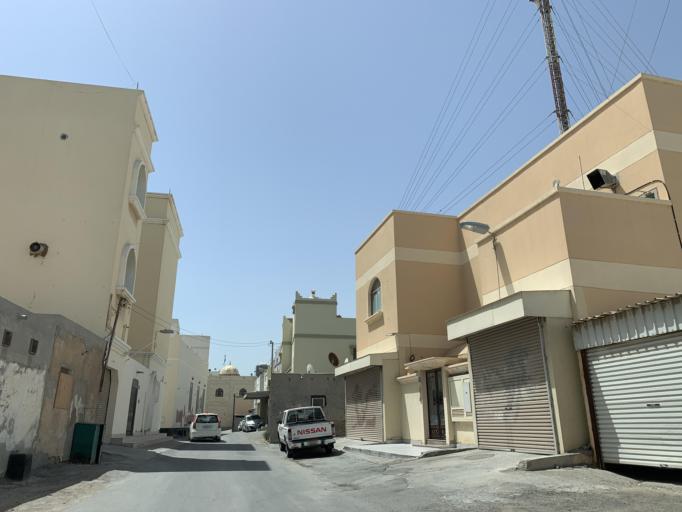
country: BH
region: Northern
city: Sitrah
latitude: 26.1444
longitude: 50.6109
